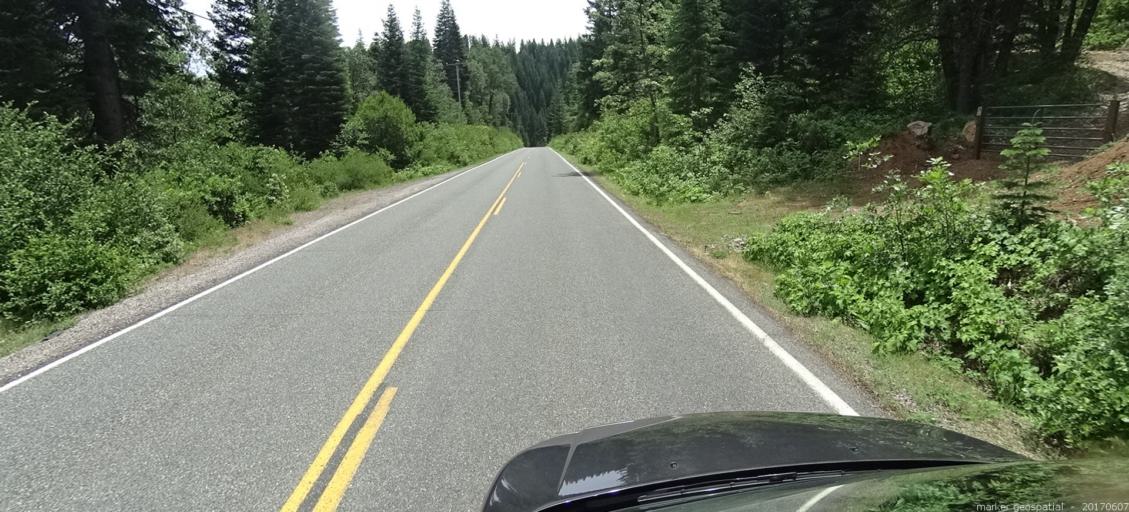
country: US
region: California
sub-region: Siskiyou County
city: Mount Shasta
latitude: 41.2719
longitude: -122.3425
